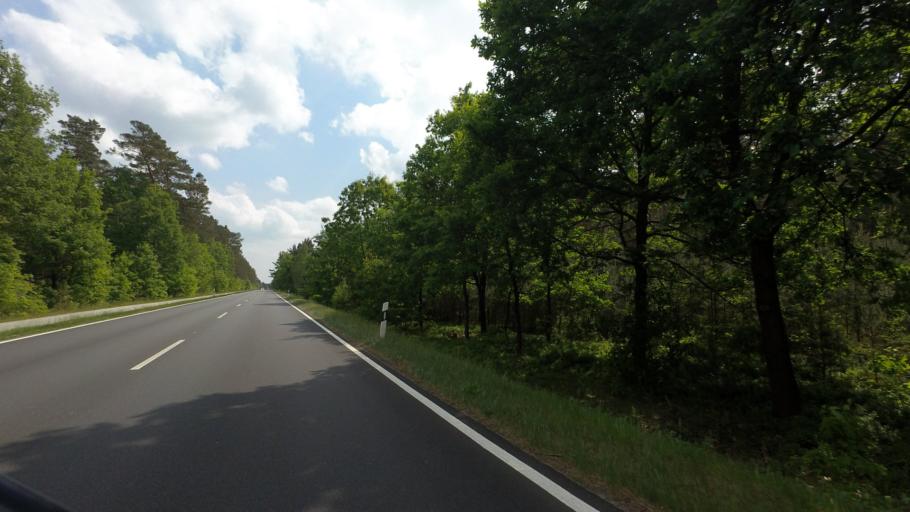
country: DE
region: Saxony
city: Niesky
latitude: 51.3439
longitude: 14.8058
